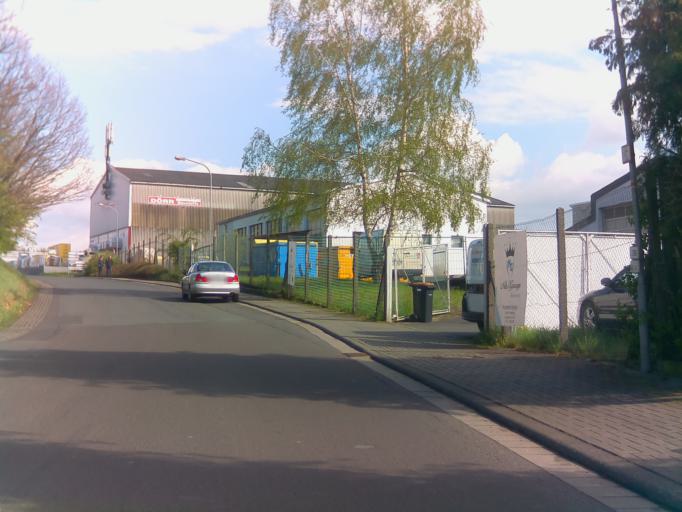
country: DE
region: Hesse
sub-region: Regierungsbezirk Giessen
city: Hoernsheim
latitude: 50.5108
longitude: 8.6252
